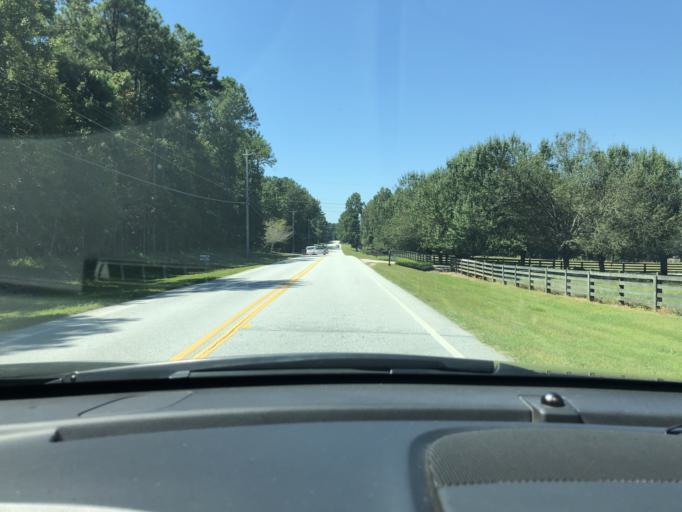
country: US
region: Georgia
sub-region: Gwinnett County
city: Grayson
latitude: 33.9038
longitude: -83.8916
